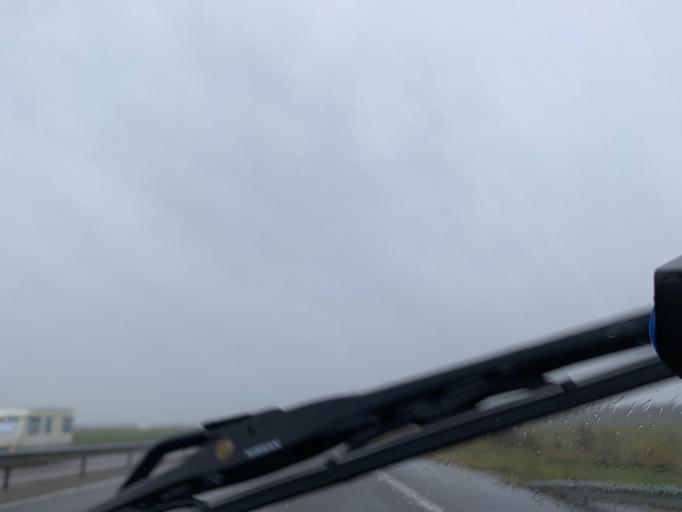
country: FR
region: Haute-Normandie
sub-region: Departement de l'Eure
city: Evreux
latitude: 48.9330
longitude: 1.2078
